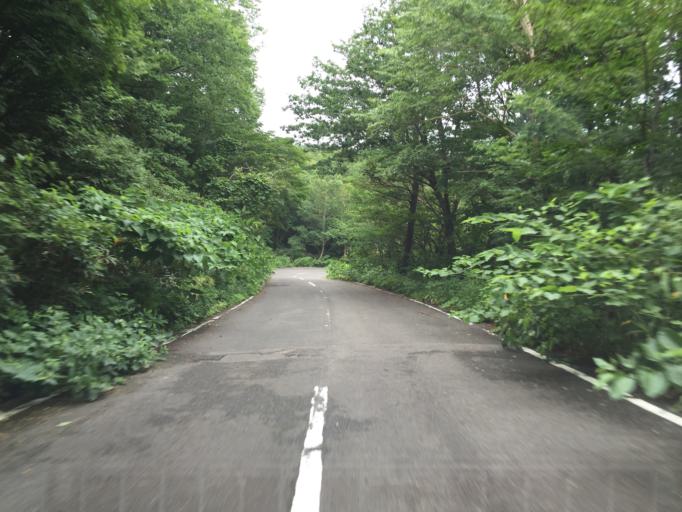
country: JP
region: Fukushima
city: Nihommatsu
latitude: 37.6577
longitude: 140.3023
